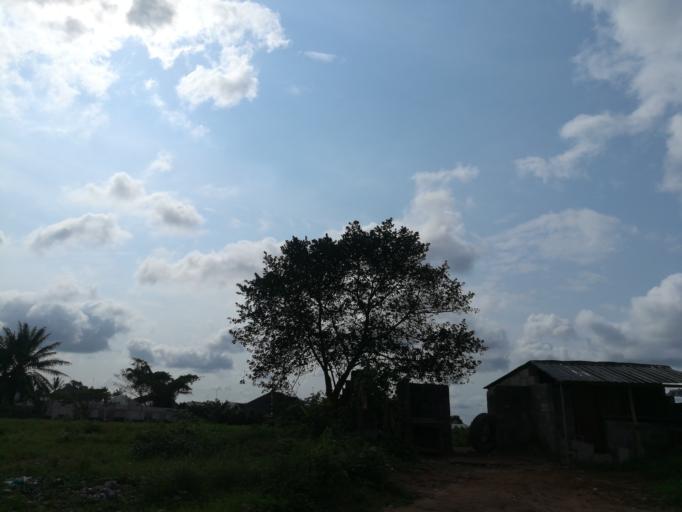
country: NG
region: Rivers
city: Okrika
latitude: 4.7620
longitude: 7.0934
